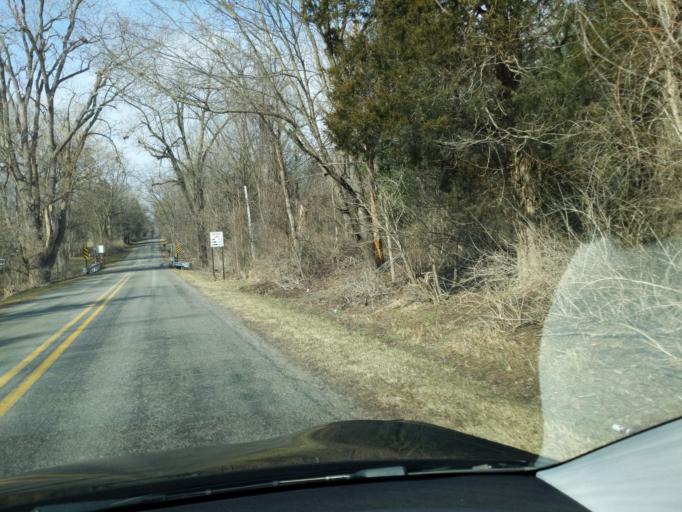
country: US
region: Michigan
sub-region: Ingham County
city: Williamston
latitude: 42.6589
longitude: -84.2878
